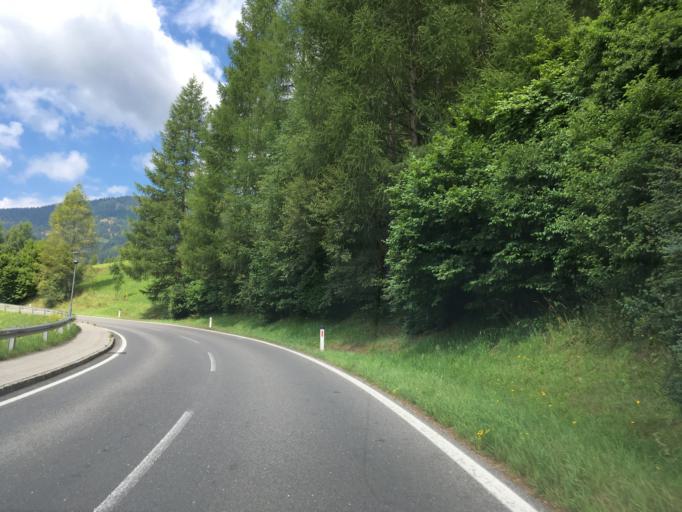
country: AT
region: Carinthia
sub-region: Politischer Bezirk Spittal an der Drau
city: Kleinkirchheim
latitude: 46.8154
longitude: 13.7914
